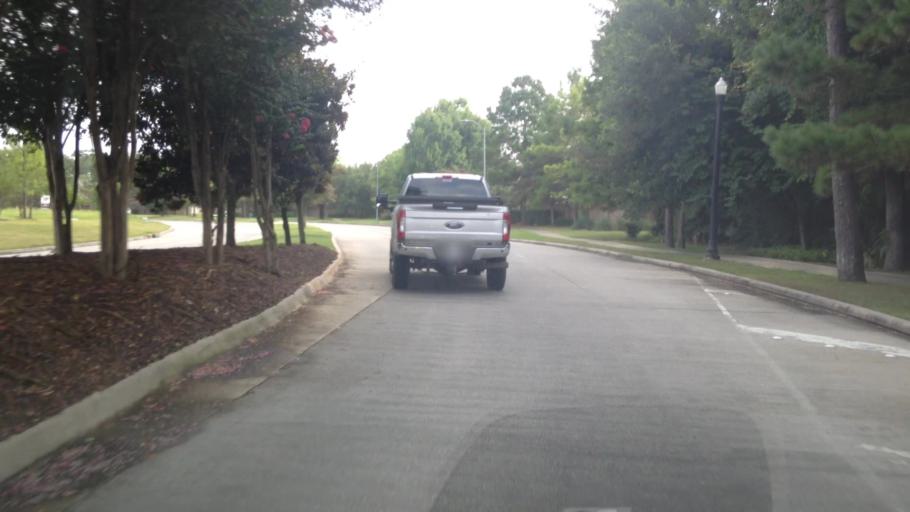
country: US
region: Texas
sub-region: Harris County
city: Atascocita
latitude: 29.9251
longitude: -95.1957
